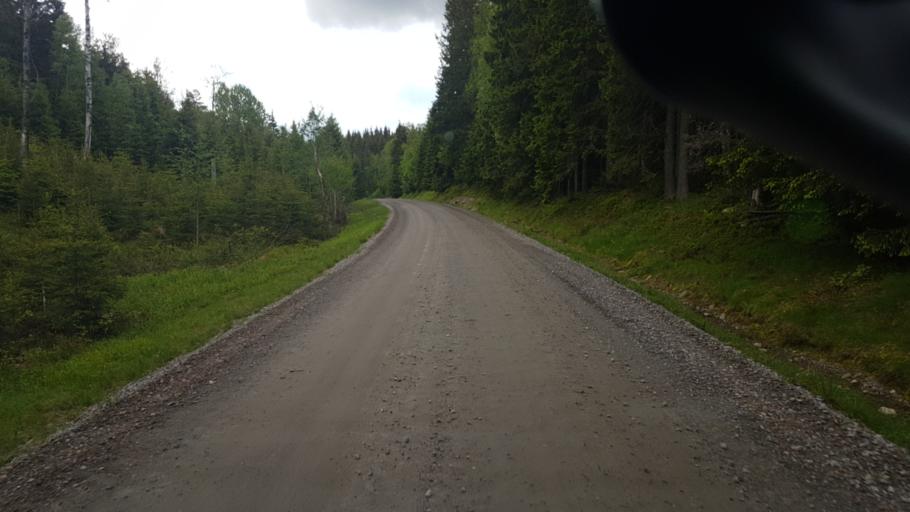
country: NO
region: Ostfold
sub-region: Romskog
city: Romskog
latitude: 59.7142
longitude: 11.9994
